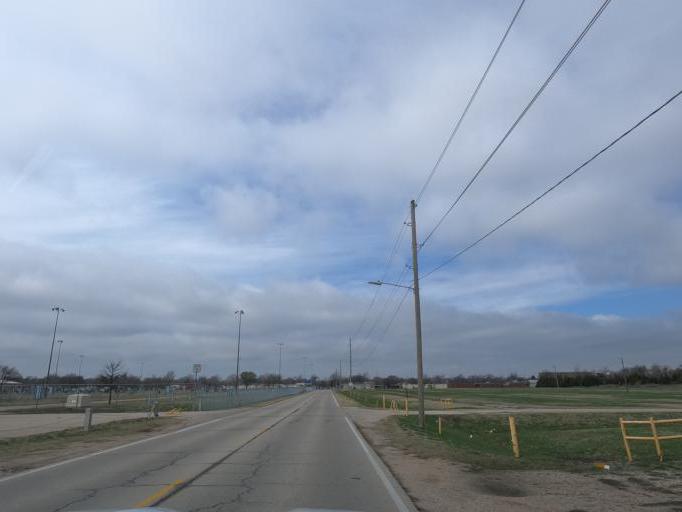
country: US
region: Kansas
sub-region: Reno County
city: Hutchinson
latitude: 38.0811
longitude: -97.9267
